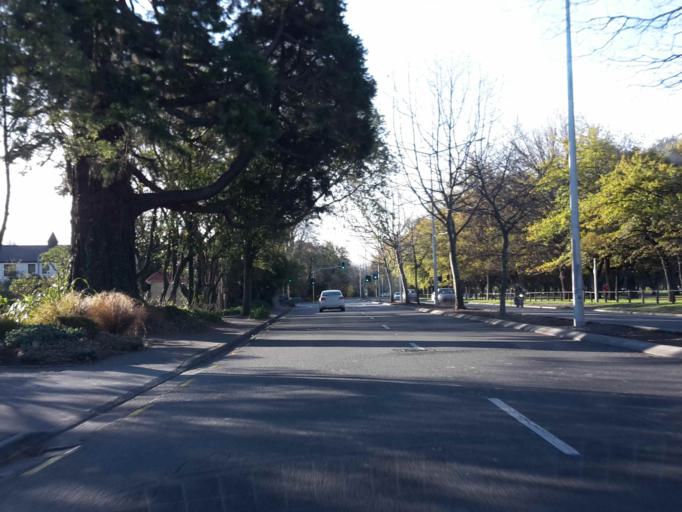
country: NZ
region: Canterbury
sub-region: Christchurch City
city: Christchurch
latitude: -43.5280
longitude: 172.6122
